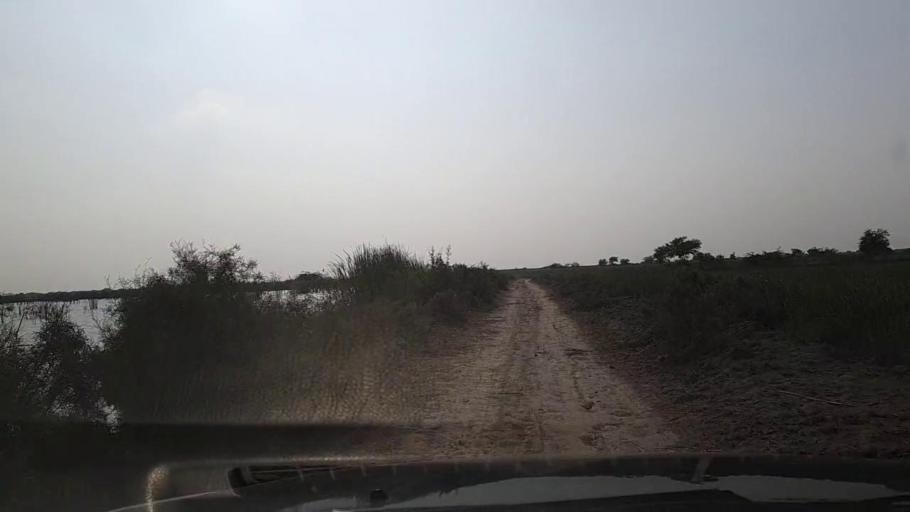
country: PK
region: Sindh
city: Mirpur Batoro
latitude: 24.6495
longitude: 68.2870
